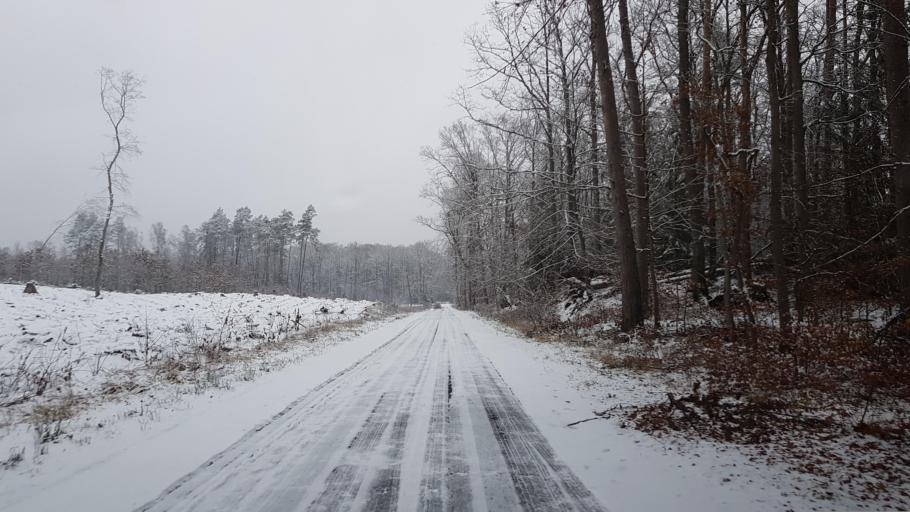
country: PL
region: West Pomeranian Voivodeship
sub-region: Powiat lobeski
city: Resko
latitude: 53.7877
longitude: 15.5322
